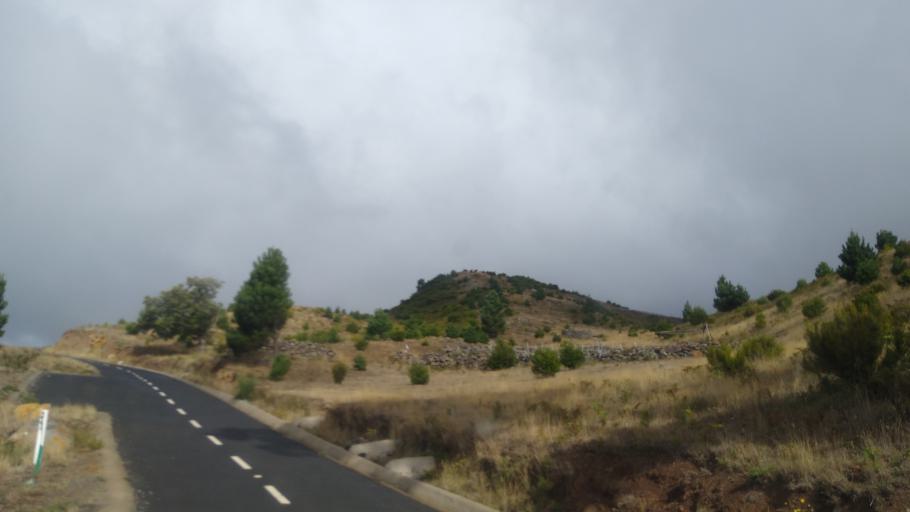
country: PT
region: Madeira
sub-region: Camara de Lobos
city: Curral das Freiras
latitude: 32.7034
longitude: -16.9391
